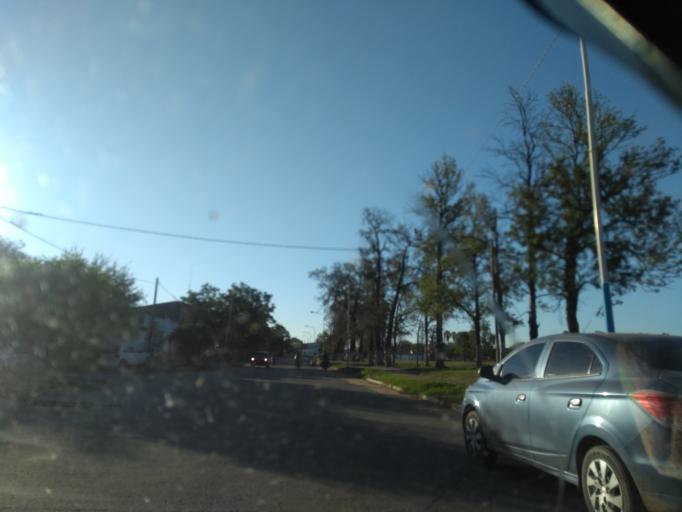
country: AR
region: Chaco
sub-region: Departamento de Quitilipi
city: Quitilipi
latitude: -26.8734
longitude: -60.2193
